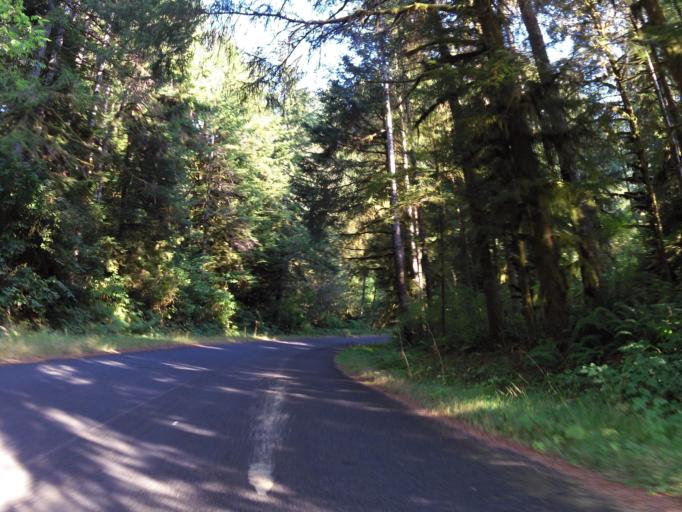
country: US
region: Oregon
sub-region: Lincoln County
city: Rose Lodge
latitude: 45.0395
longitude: -123.9116
